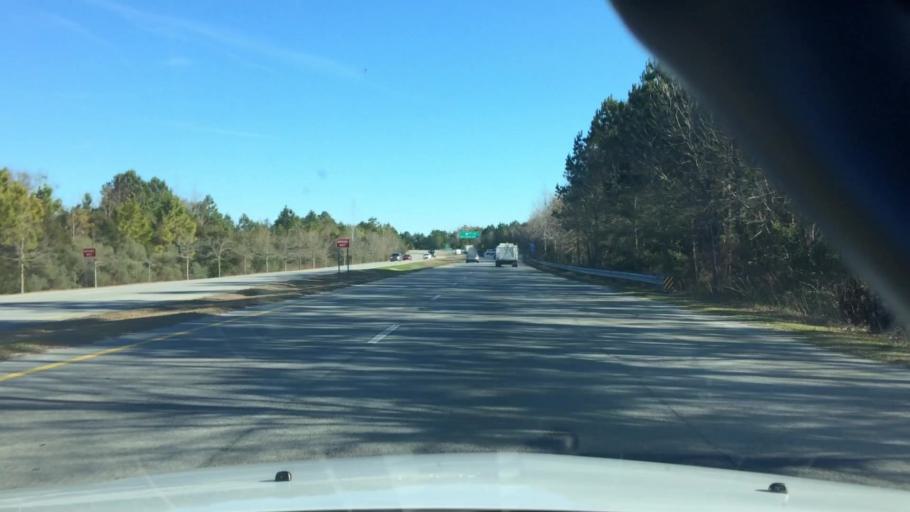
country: US
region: South Carolina
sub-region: Horry County
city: Myrtle Beach
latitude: 33.7346
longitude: -78.8529
